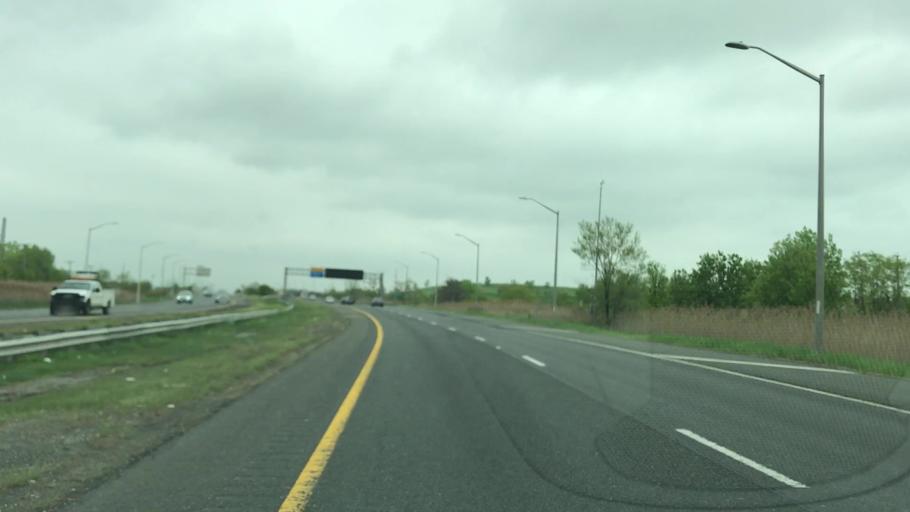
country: US
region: New Jersey
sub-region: Middlesex County
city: Carteret
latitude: 40.5731
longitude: -74.1898
